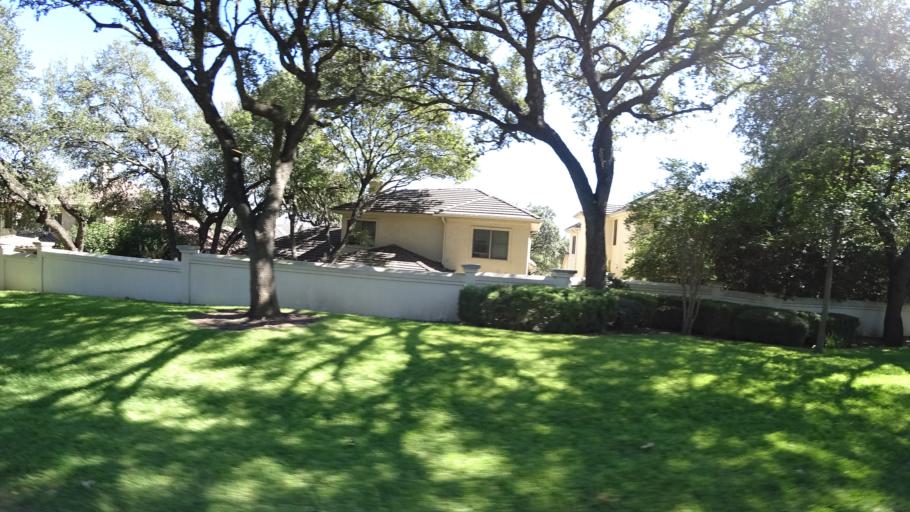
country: US
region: Texas
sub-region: Travis County
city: West Lake Hills
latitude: 30.3059
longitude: -97.7867
